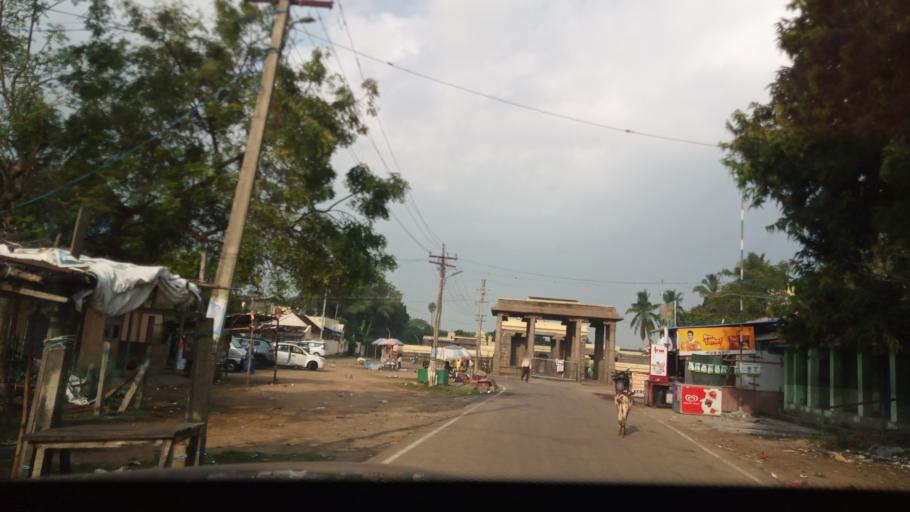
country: IN
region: Tamil Nadu
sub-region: Kancheepuram
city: Mamallapuram
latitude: 12.7630
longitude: 80.2432
